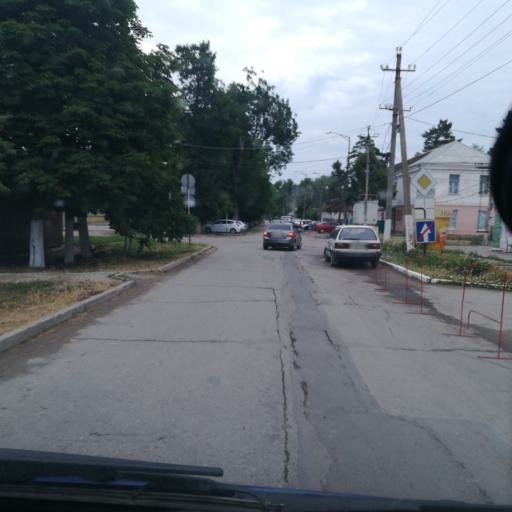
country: RU
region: Krasnodarskiy
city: Slavyansk-na-Kubani
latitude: 45.2637
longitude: 38.1291
